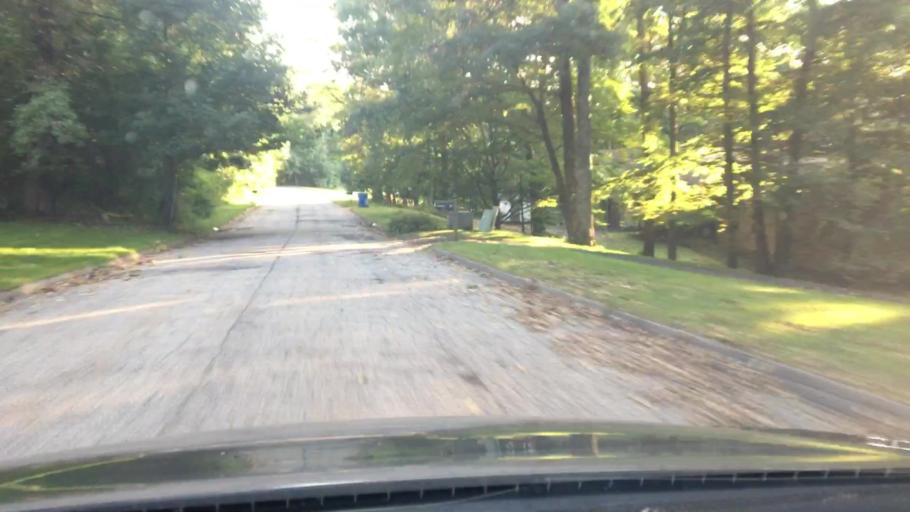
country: US
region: Connecticut
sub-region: Litchfield County
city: New Milford
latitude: 41.6027
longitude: -73.3890
